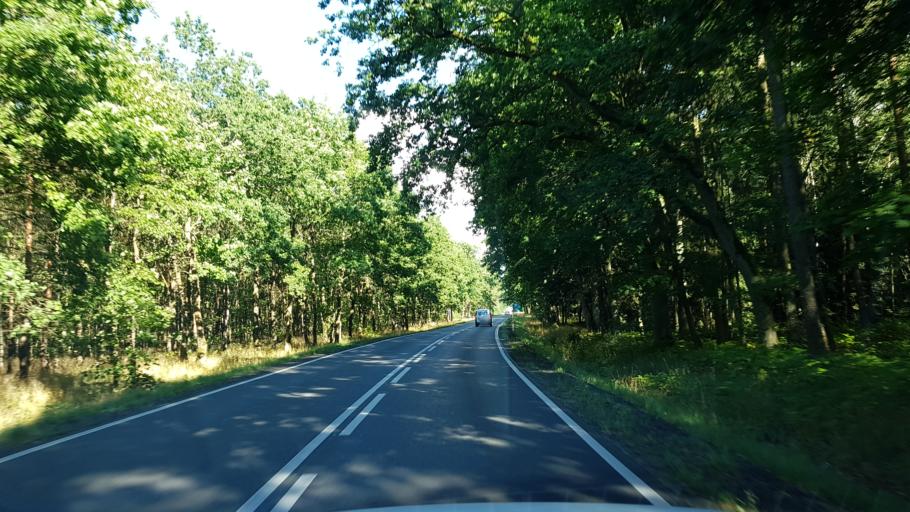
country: PL
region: West Pomeranian Voivodeship
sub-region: Powiat goleniowski
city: Goleniow
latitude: 53.5749
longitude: 14.7830
